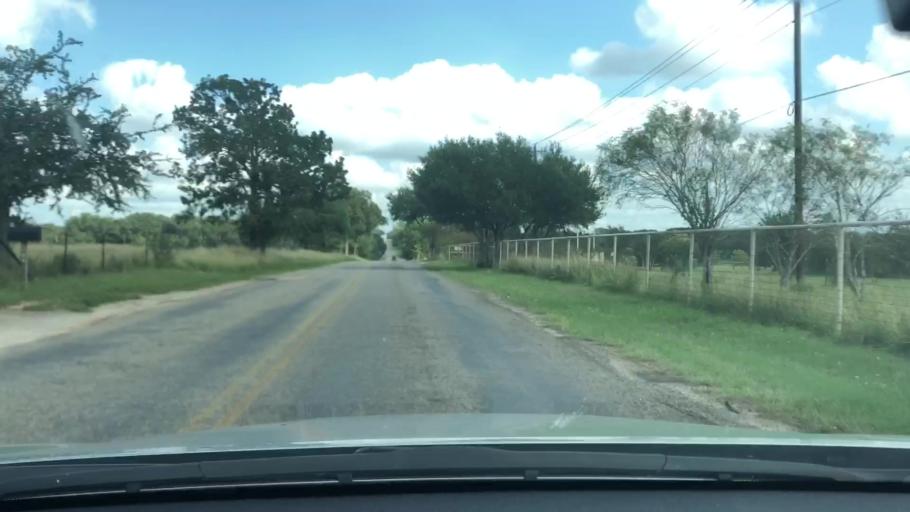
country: US
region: Texas
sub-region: Bexar County
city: Fair Oaks Ranch
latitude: 29.7863
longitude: -98.6706
